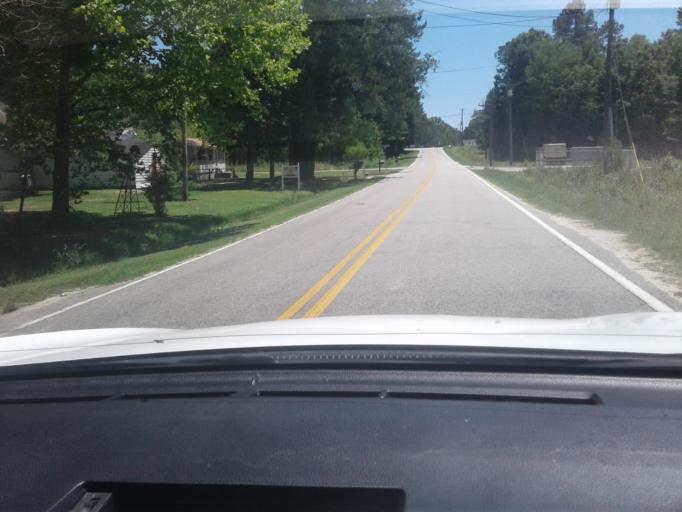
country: US
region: North Carolina
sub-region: Harnett County
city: Erwin
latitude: 35.3202
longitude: -78.7224
